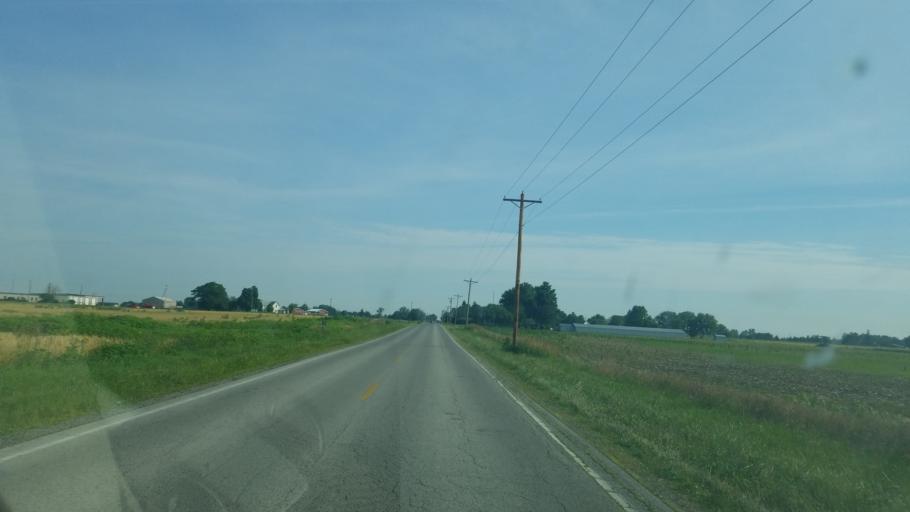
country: US
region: Ohio
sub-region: Hancock County
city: Findlay
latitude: 40.9993
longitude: -83.6985
